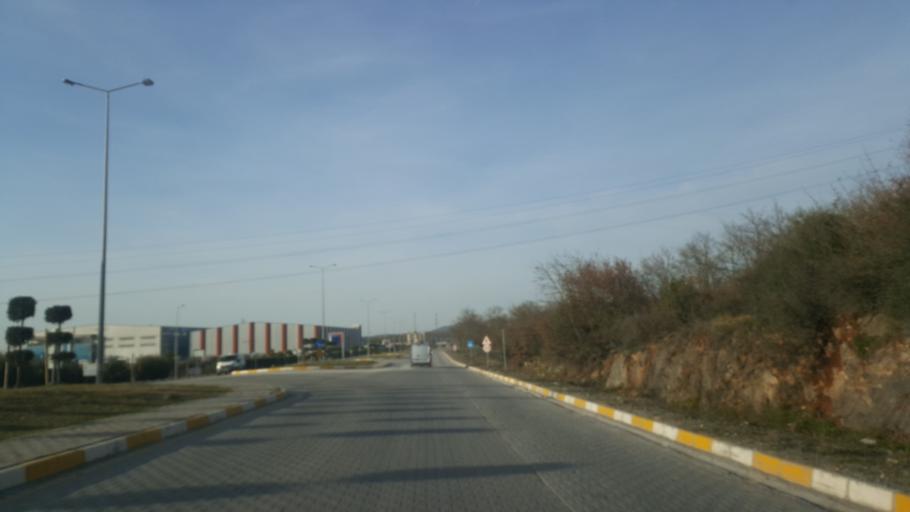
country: TR
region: Kocaeli
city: Tavsanli
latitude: 40.8646
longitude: 29.5596
